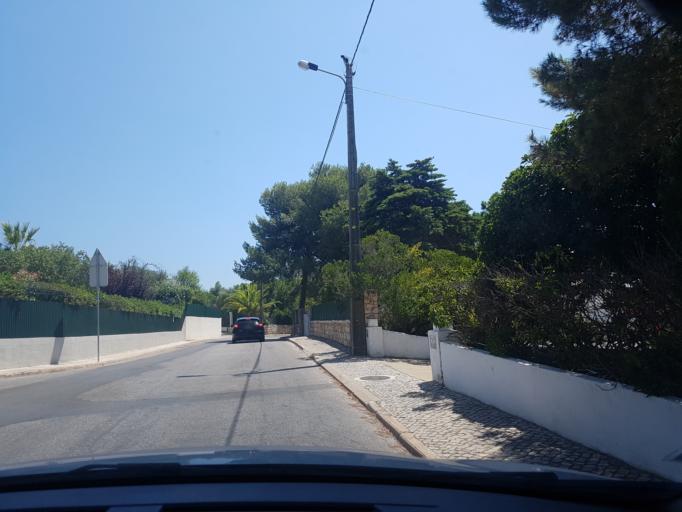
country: PT
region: Faro
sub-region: Lagoa
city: Carvoeiro
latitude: 37.0989
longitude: -8.4584
